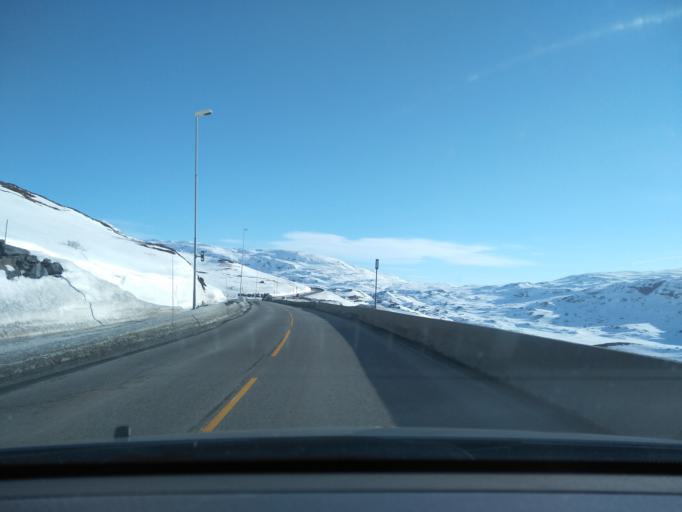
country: NO
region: Hordaland
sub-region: Odda
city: Odda
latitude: 59.8462
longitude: 6.9698
